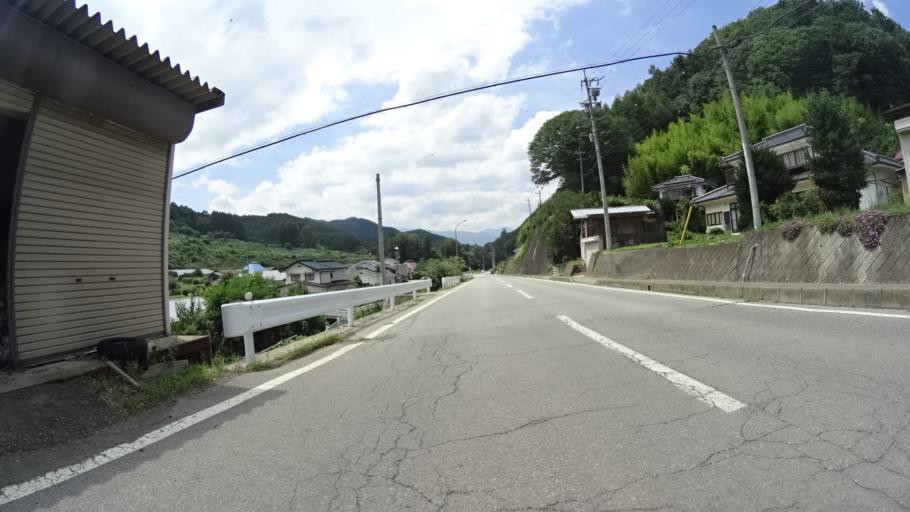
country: JP
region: Nagano
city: Saku
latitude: 36.0592
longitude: 138.5500
